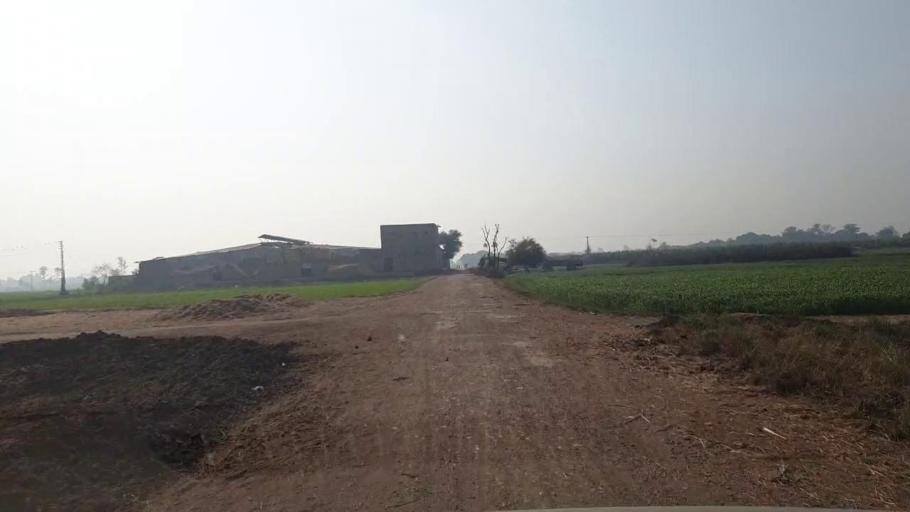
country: PK
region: Sindh
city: Sakrand
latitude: 25.9992
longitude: 68.3674
